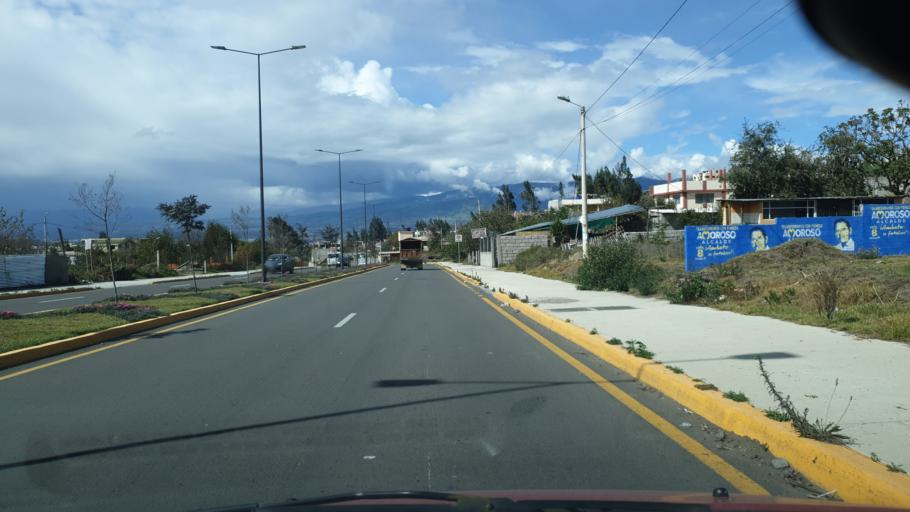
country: EC
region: Tungurahua
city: Ambato
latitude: -1.2957
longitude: -78.6344
